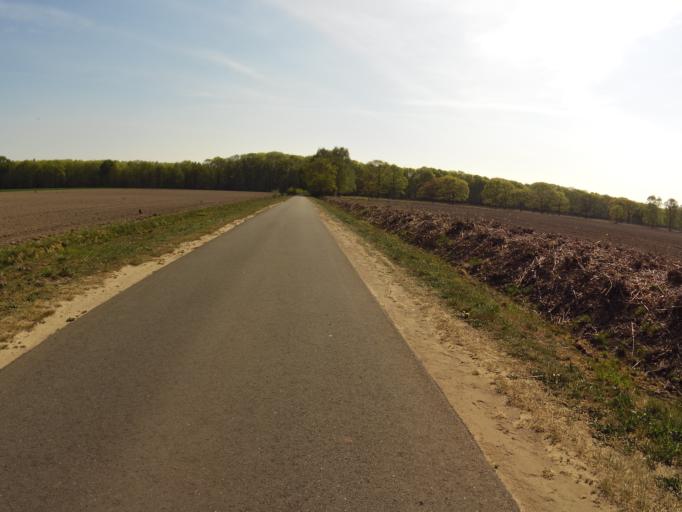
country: NL
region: North Brabant
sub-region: Gemeente Heusden
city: Heusden
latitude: 51.6724
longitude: 5.1755
